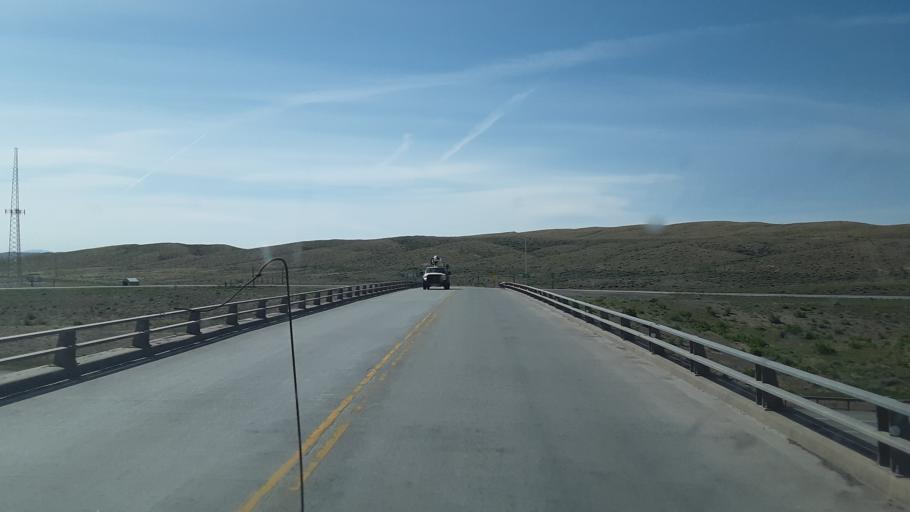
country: US
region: Wyoming
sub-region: Carbon County
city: Rawlins
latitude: 41.7727
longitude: -107.0825
